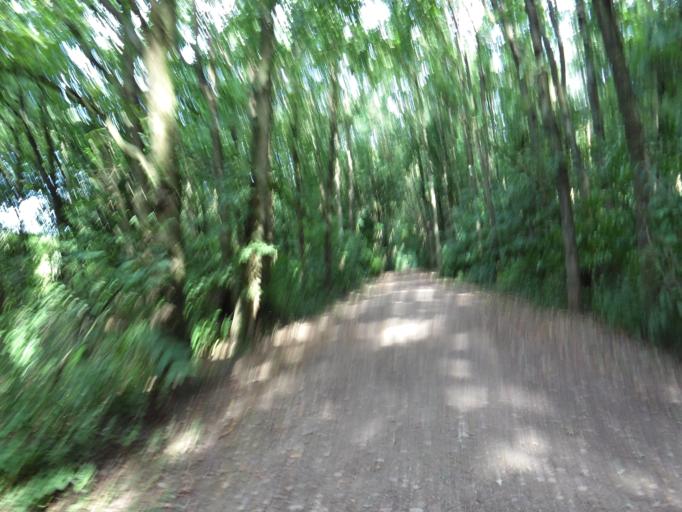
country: DE
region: North Rhine-Westphalia
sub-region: Regierungsbezirk Koln
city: Alsdorf
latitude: 50.8521
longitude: 6.1946
